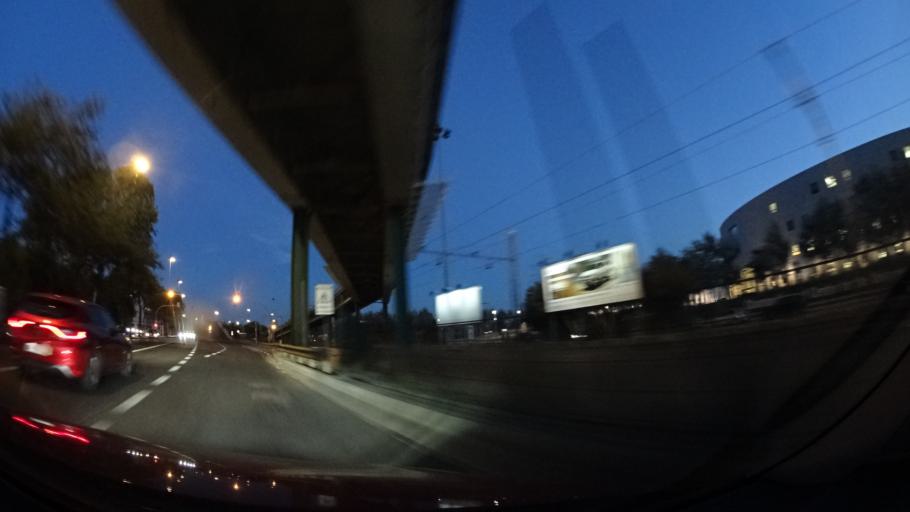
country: PT
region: Lisbon
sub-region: Oeiras
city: Alges
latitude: 38.6946
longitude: -9.2213
